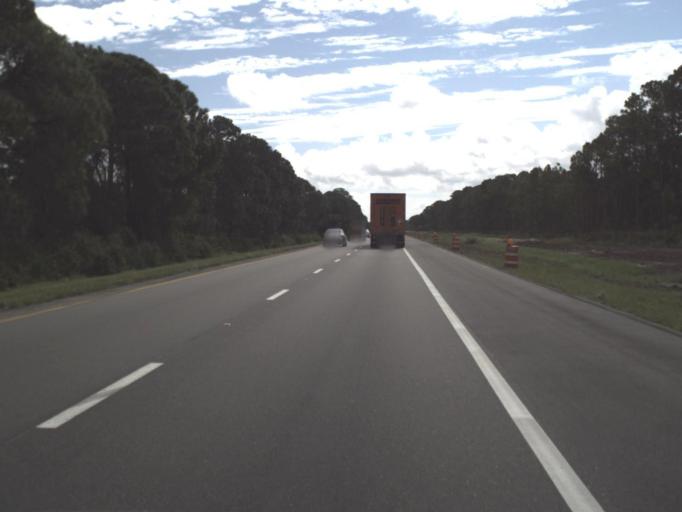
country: US
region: Florida
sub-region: Sarasota County
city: Warm Mineral Springs
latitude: 27.0997
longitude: -82.2621
